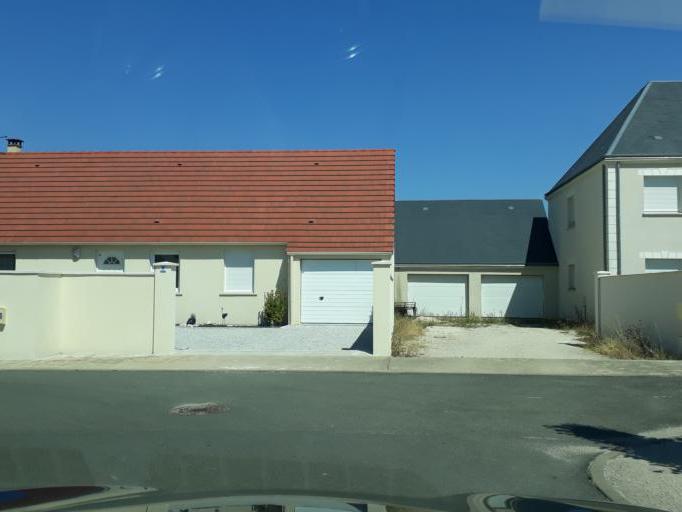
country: FR
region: Centre
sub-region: Departement du Loiret
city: Saran
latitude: 47.9869
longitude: 1.8933
